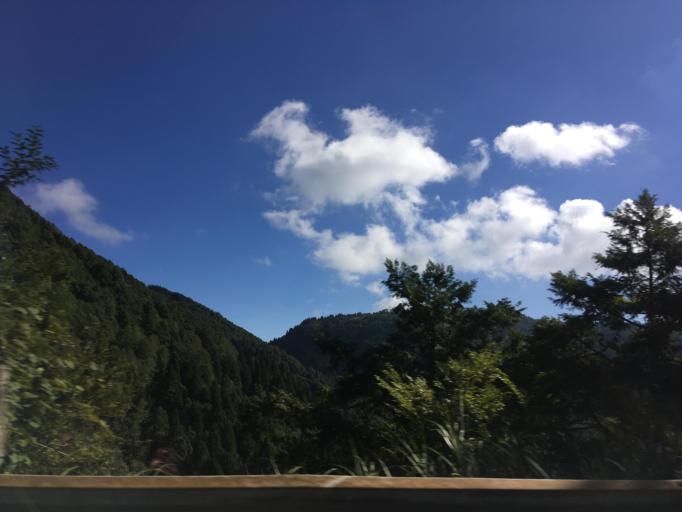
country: TW
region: Taiwan
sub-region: Yilan
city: Yilan
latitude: 24.5105
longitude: 121.5691
